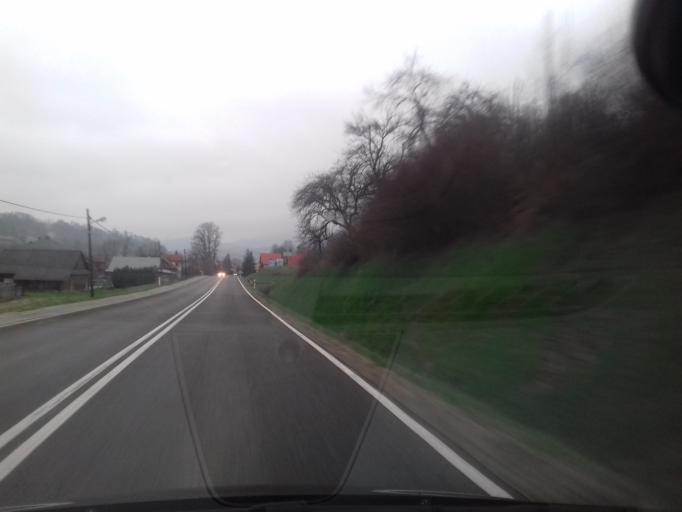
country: PL
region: Lesser Poland Voivodeship
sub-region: Powiat limanowski
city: Mszana Gorna
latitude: 49.6839
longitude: 20.1037
